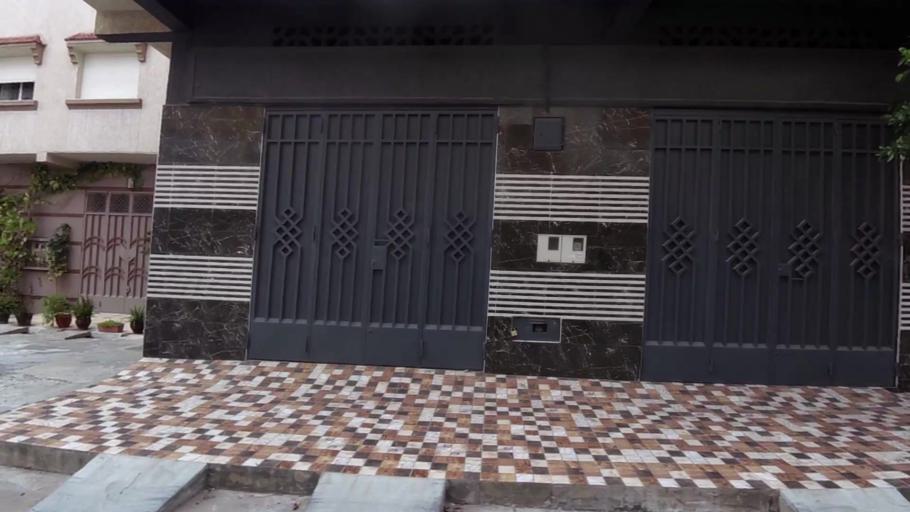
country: MA
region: Tanger-Tetouan
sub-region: Tanger-Assilah
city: Tangier
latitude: 35.7580
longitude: -5.8001
